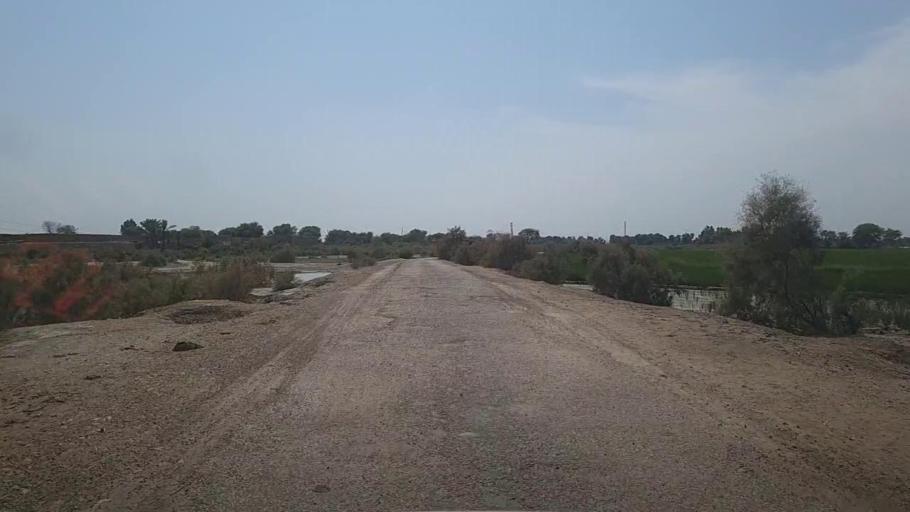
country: PK
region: Sindh
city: Kandhkot
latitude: 28.3105
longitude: 69.2055
